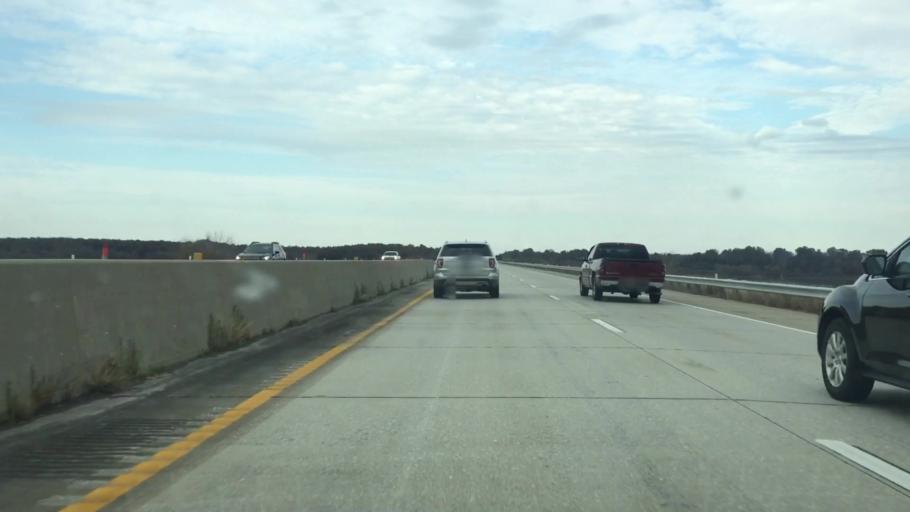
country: US
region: Missouri
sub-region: Henry County
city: Clinton
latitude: 38.2803
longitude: -93.7595
